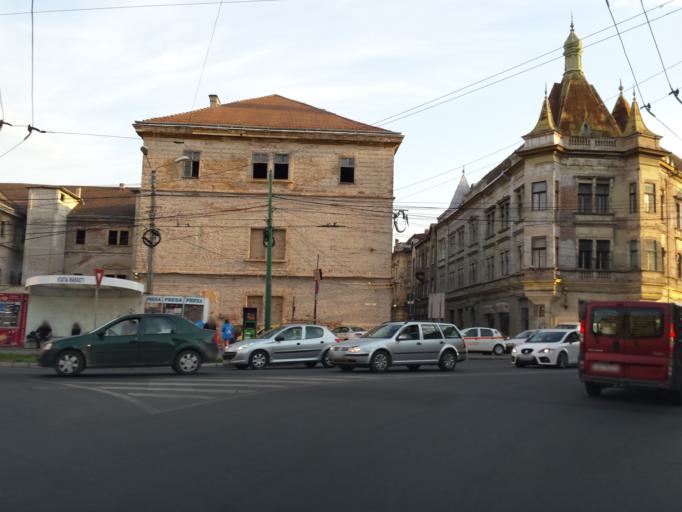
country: RO
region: Timis
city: Timisoara
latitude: 45.7595
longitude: 21.2276
